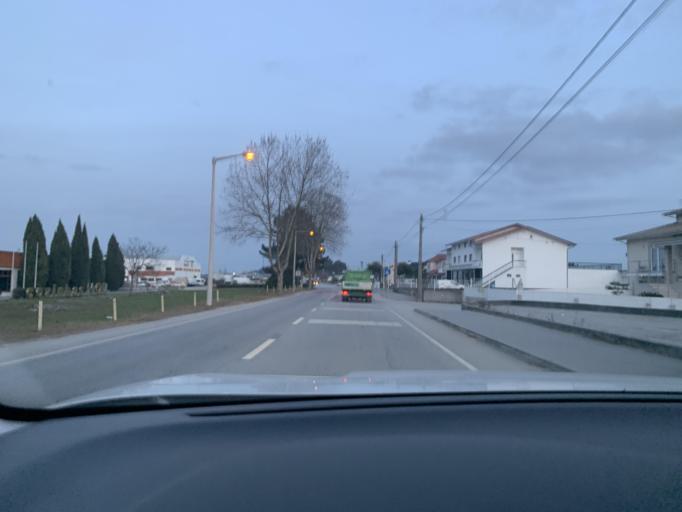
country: PT
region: Viseu
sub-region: Viseu
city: Rio de Loba
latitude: 40.6275
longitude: -7.8781
